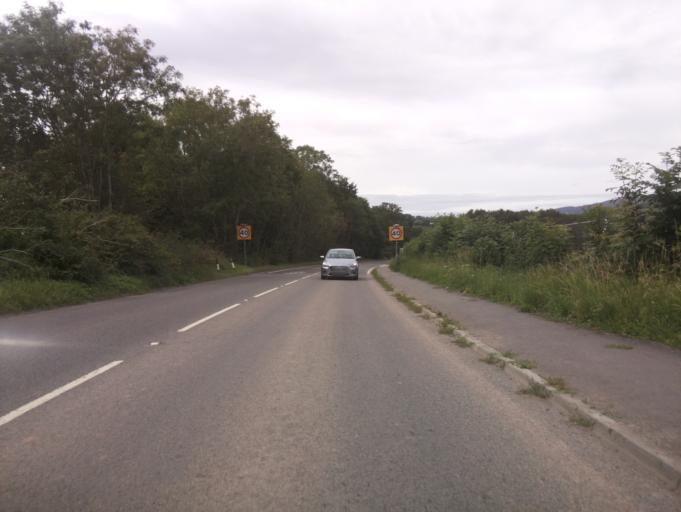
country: GB
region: England
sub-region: Somerset
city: Wells
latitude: 51.2090
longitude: -2.6687
